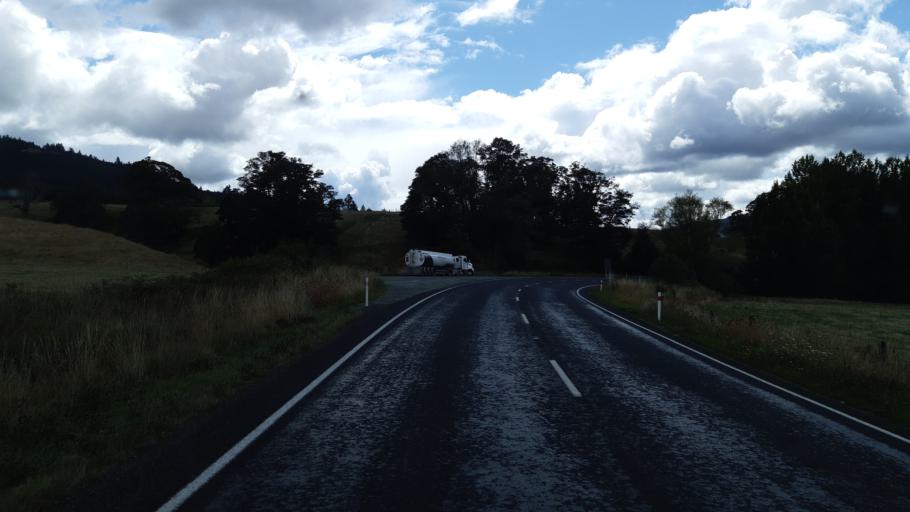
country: NZ
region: Tasman
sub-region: Tasman District
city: Wakefield
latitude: -41.5568
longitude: 172.7857
